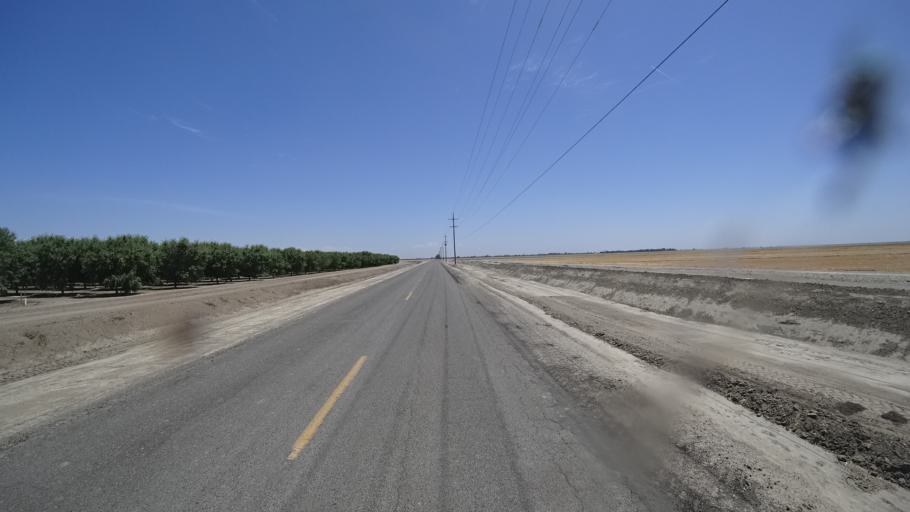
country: US
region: California
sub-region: Kings County
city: Corcoran
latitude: 36.1089
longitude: -119.6209
